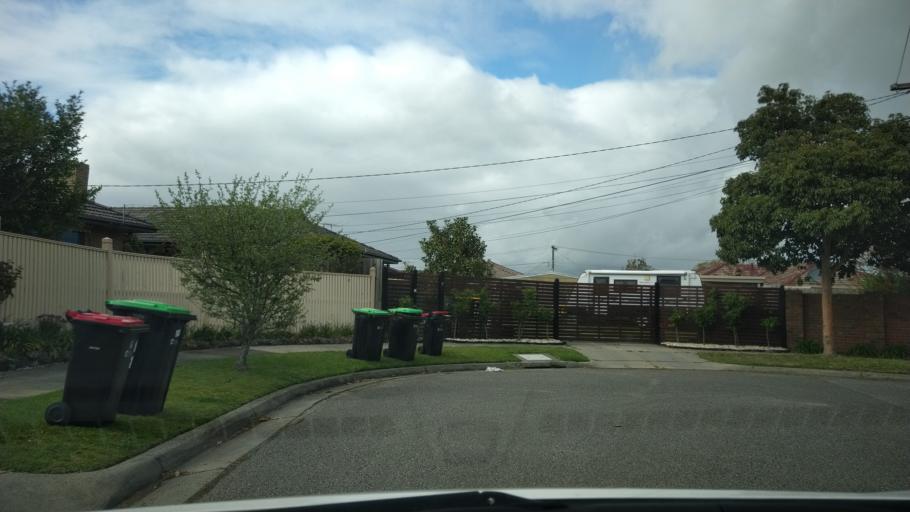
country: AU
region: Victoria
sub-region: Greater Dandenong
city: Keysborough
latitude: -37.9887
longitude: 145.1768
